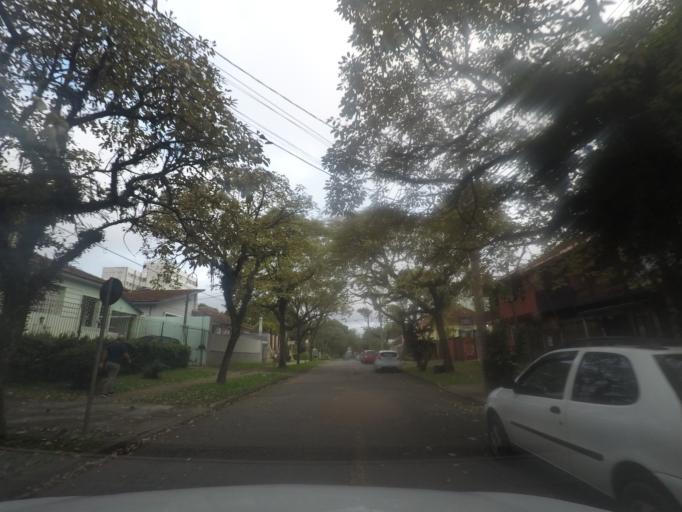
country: BR
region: Parana
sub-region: Curitiba
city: Curitiba
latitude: -25.4288
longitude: -49.2478
